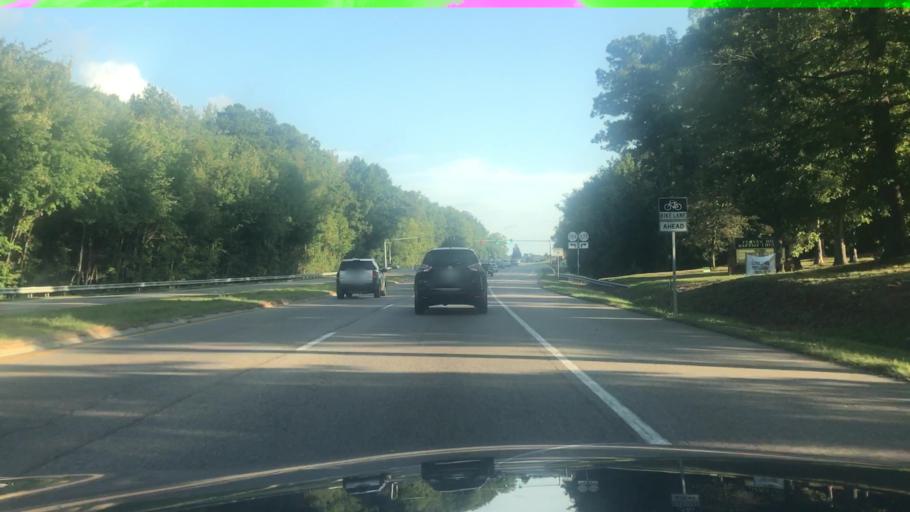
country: US
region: Virginia
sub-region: Chesterfield County
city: Brandermill
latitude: 37.4499
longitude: -77.5850
